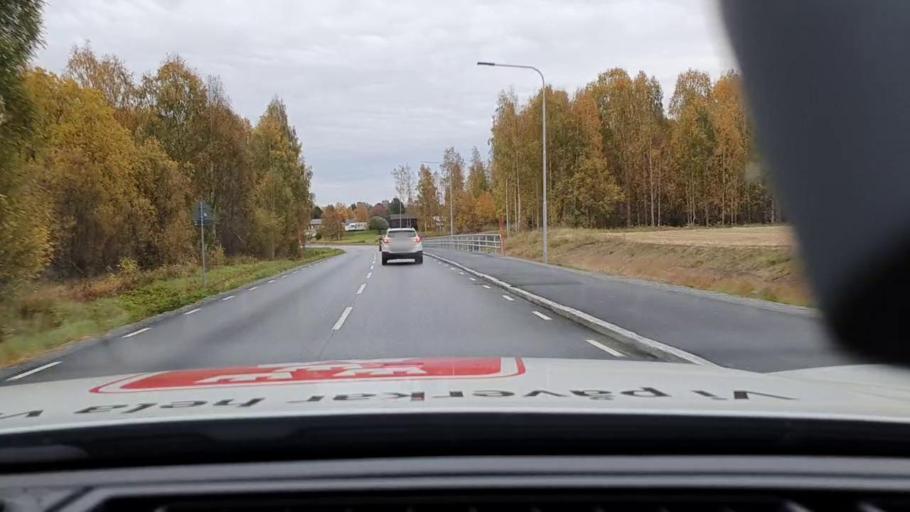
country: SE
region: Norrbotten
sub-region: Bodens Kommun
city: Saevast
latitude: 65.7682
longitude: 21.7184
